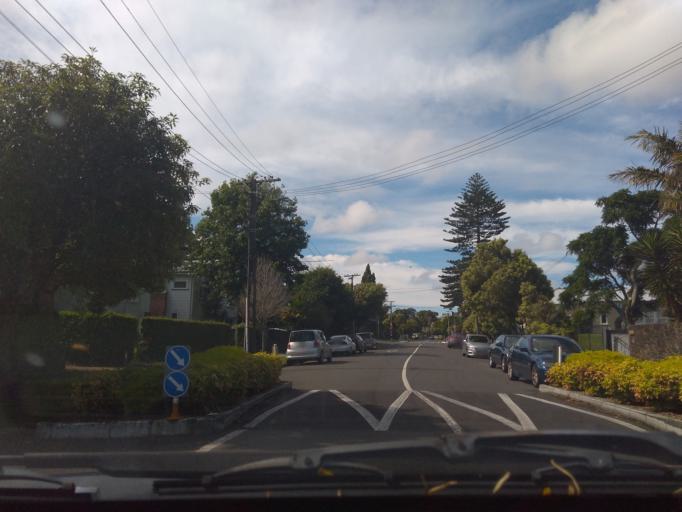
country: NZ
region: Auckland
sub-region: Auckland
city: Auckland
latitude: -36.8806
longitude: 174.7265
